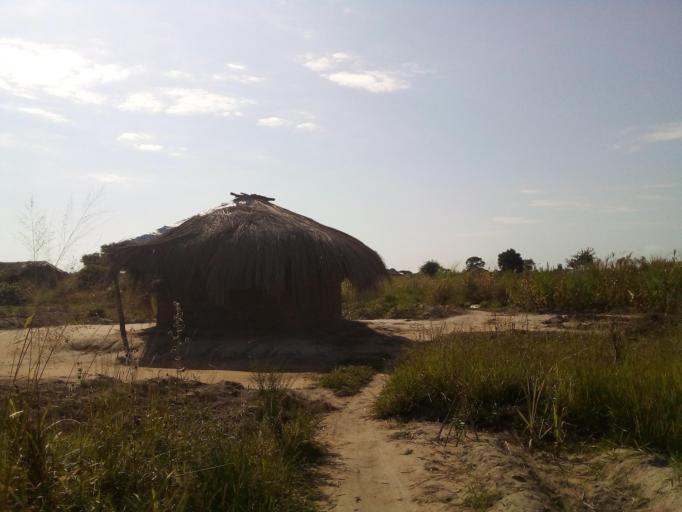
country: MZ
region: Zambezia
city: Quelimane
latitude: -17.5535
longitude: 36.7045
